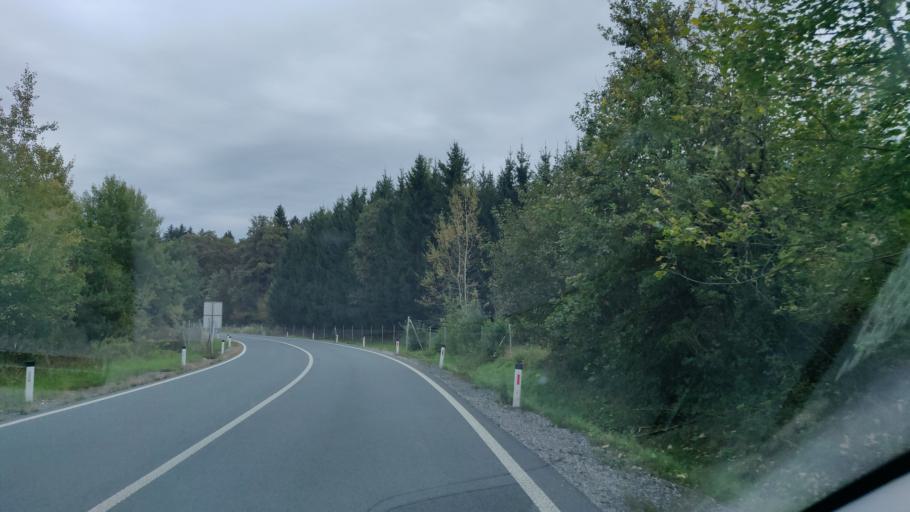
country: SI
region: Kranj
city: Britof
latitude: 46.2398
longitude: 14.3949
